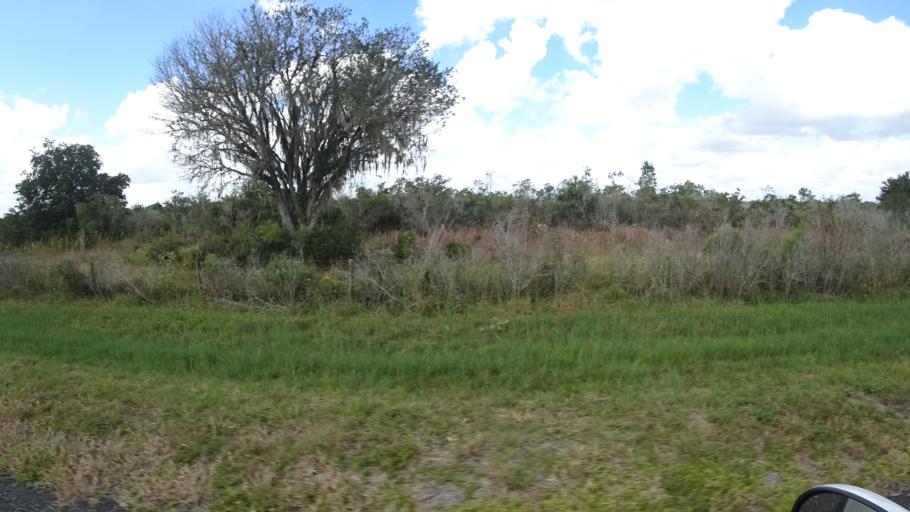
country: US
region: Florida
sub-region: Hillsborough County
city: Wimauma
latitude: 27.4790
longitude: -82.1707
